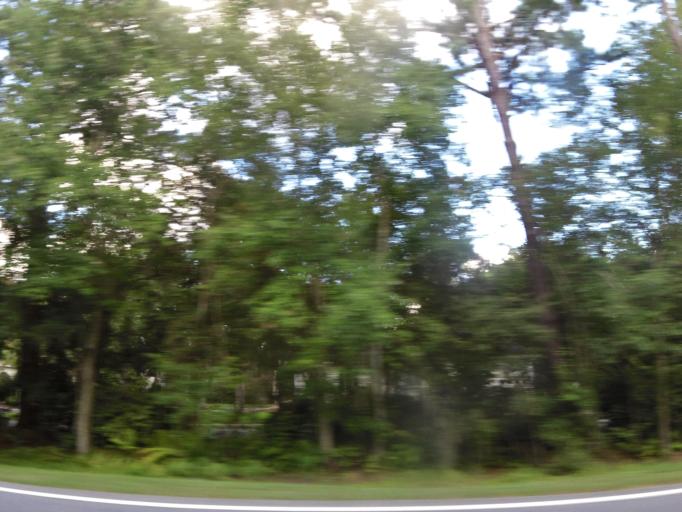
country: US
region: Georgia
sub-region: Glynn County
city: Saint Simon Mills
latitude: 31.1721
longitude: -81.4018
